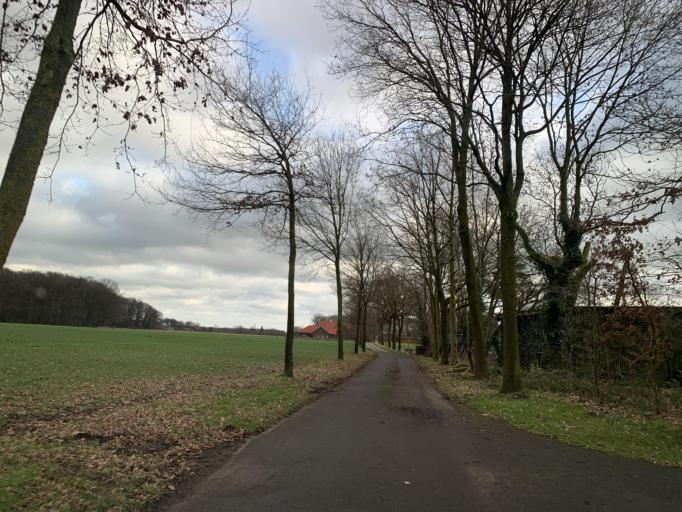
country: DE
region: North Rhine-Westphalia
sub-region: Regierungsbezirk Munster
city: Ascheberg
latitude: 51.8030
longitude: 7.5802
